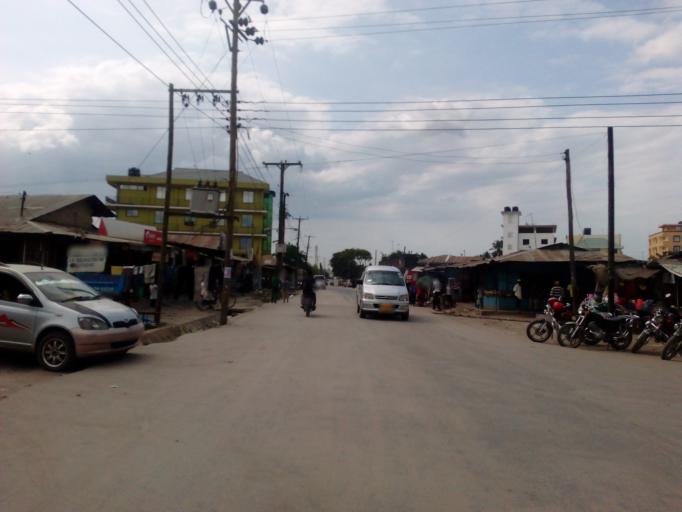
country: TZ
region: Dar es Salaam
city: Dar es Salaam
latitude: -6.8537
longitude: 39.2572
